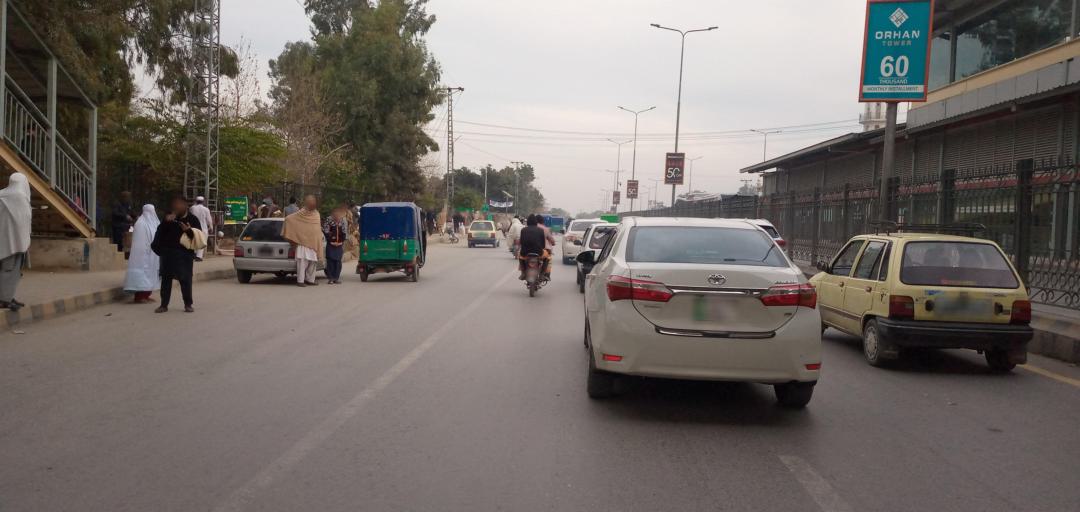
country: PK
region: Khyber Pakhtunkhwa
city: Peshawar
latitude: 33.9979
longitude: 71.4872
